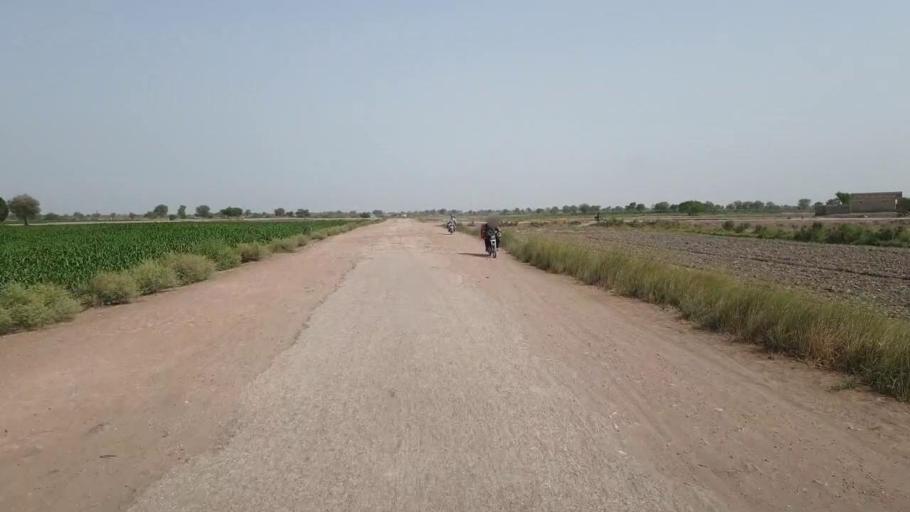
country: PK
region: Sindh
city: Daulatpur
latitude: 26.5527
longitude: 67.9913
